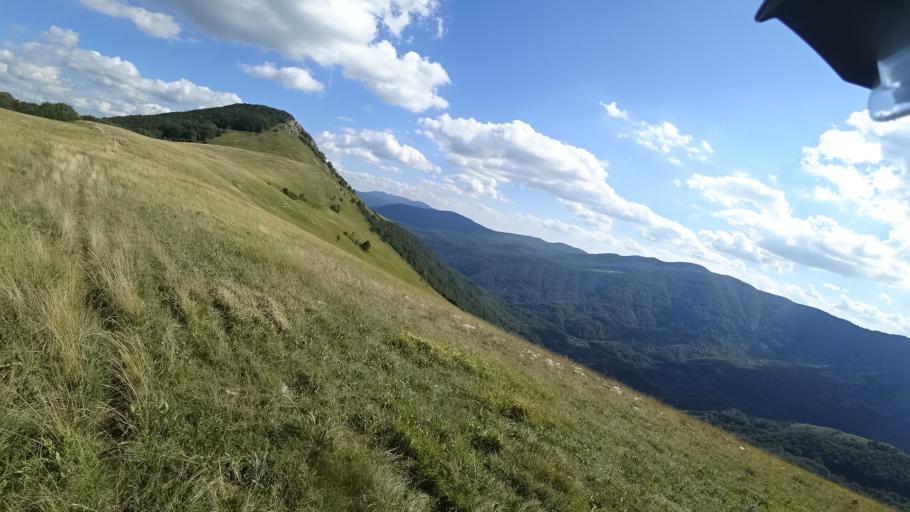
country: HR
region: Zadarska
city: Gracac
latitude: 44.3864
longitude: 16.0423
